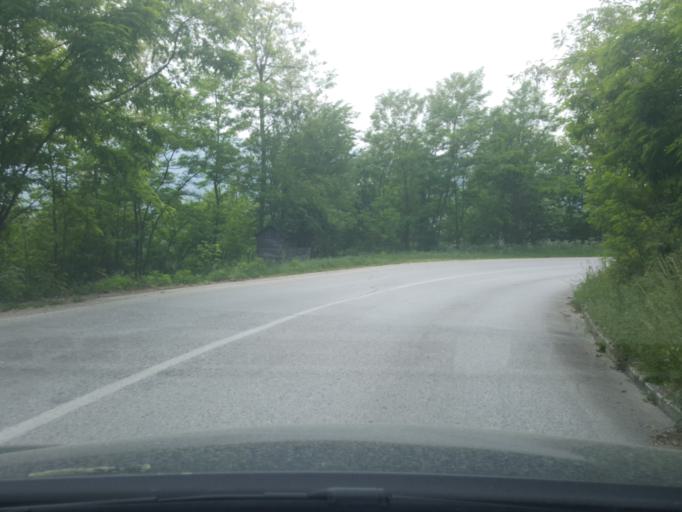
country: RS
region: Central Serbia
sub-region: Zlatiborski Okrug
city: Bajina Basta
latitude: 43.9429
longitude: 19.5614
